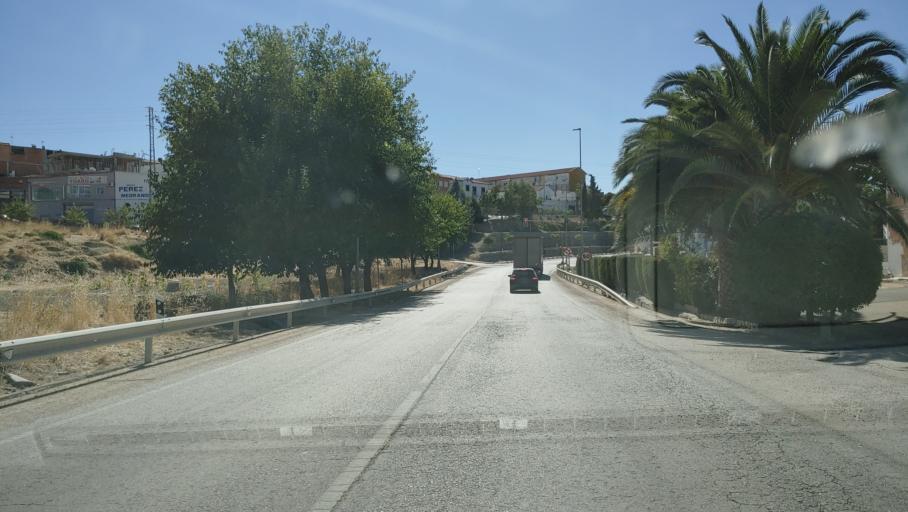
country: ES
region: Andalusia
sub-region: Provincia de Jaen
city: Villacarrillo
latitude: 38.1162
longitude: -3.0913
